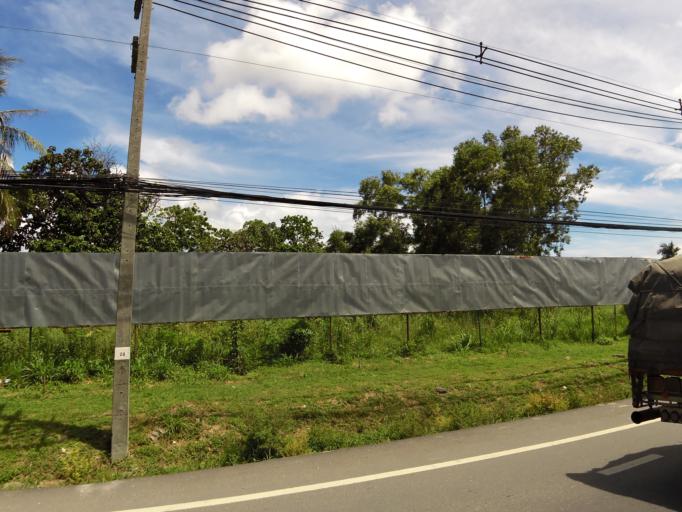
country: TH
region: Phuket
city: Ban Chalong
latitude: 7.8567
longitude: 98.3387
